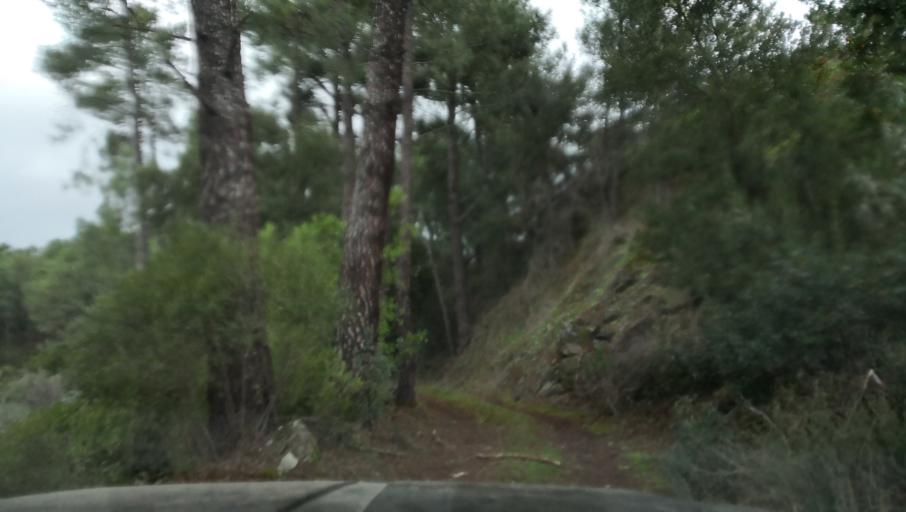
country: PT
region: Vila Real
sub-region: Vila Real
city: Vila Real
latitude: 41.2454
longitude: -7.7387
